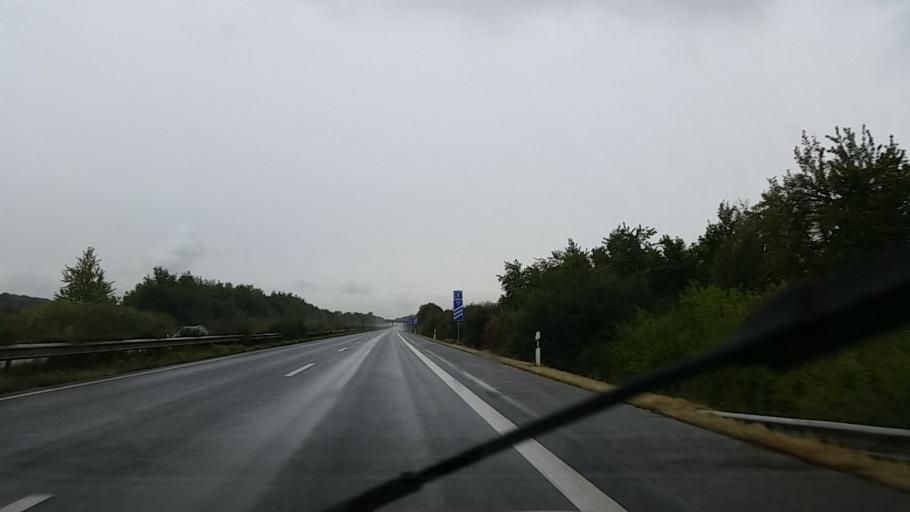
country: DE
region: Lower Saxony
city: Flothe
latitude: 52.0829
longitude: 10.4976
